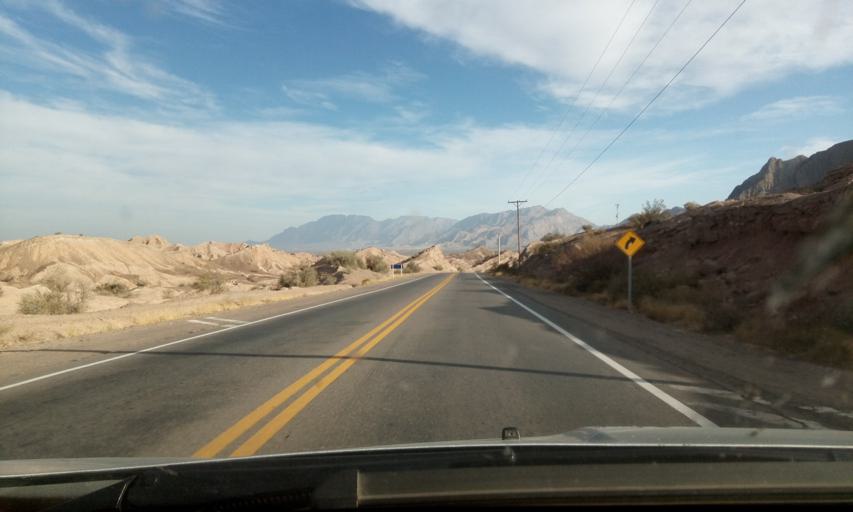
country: AR
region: San Juan
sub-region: Departamento de Rivadavia
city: Rivadavia
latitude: -31.4687
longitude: -68.6421
